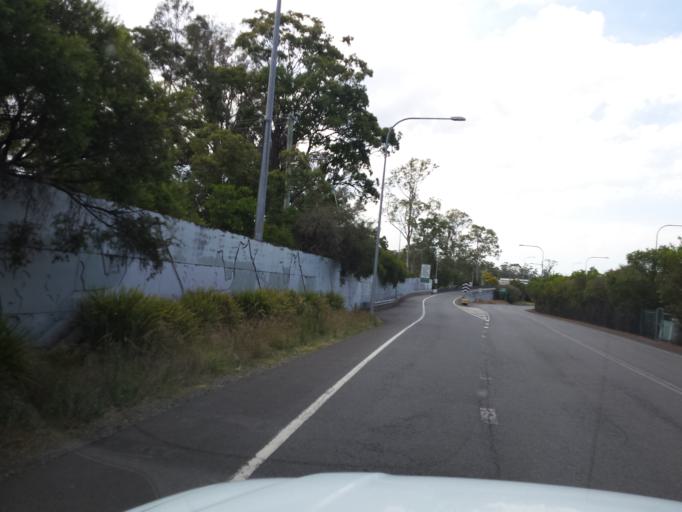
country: AU
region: Queensland
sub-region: Gold Coast
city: Nerang
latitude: -28.0038
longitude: 153.3399
